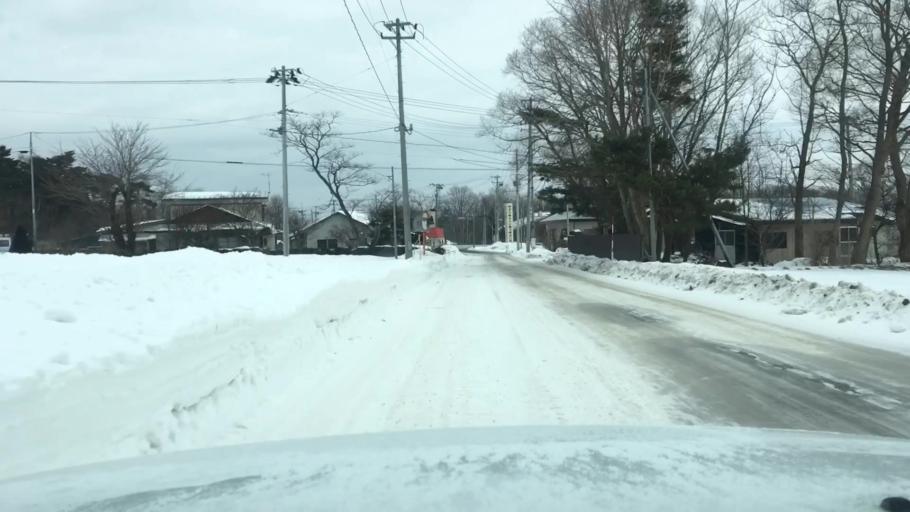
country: JP
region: Iwate
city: Shizukuishi
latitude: 39.9151
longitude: 141.0055
